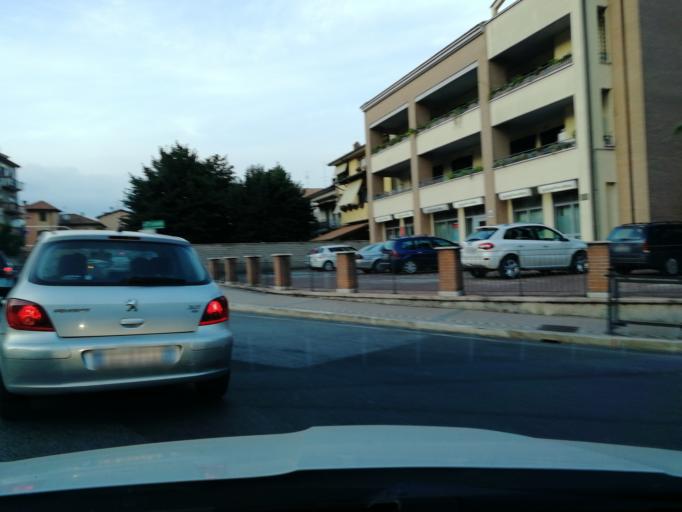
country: IT
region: Latium
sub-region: Citta metropolitana di Roma Capitale
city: Artena
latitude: 41.7418
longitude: 12.9147
